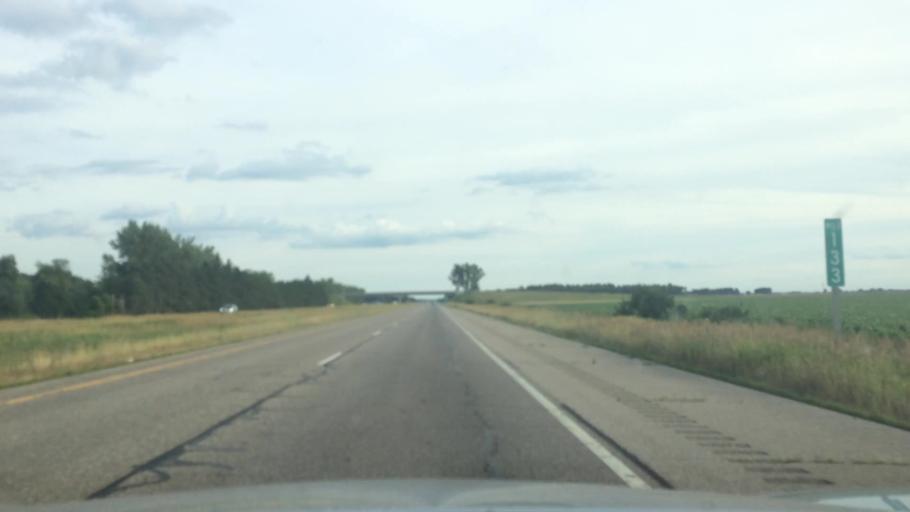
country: US
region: Wisconsin
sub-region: Waushara County
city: Wautoma
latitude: 44.1602
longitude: -89.5327
